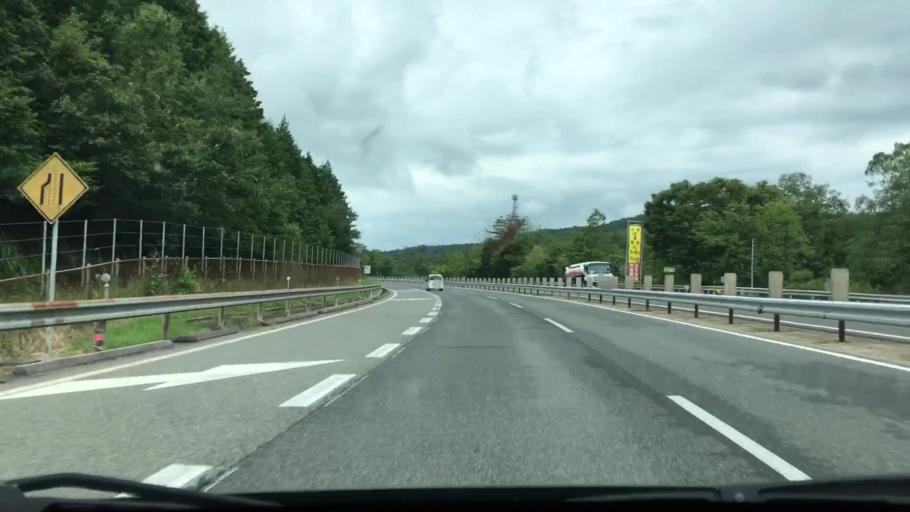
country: JP
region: Hiroshima
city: Miyoshi
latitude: 34.7570
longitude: 132.7550
